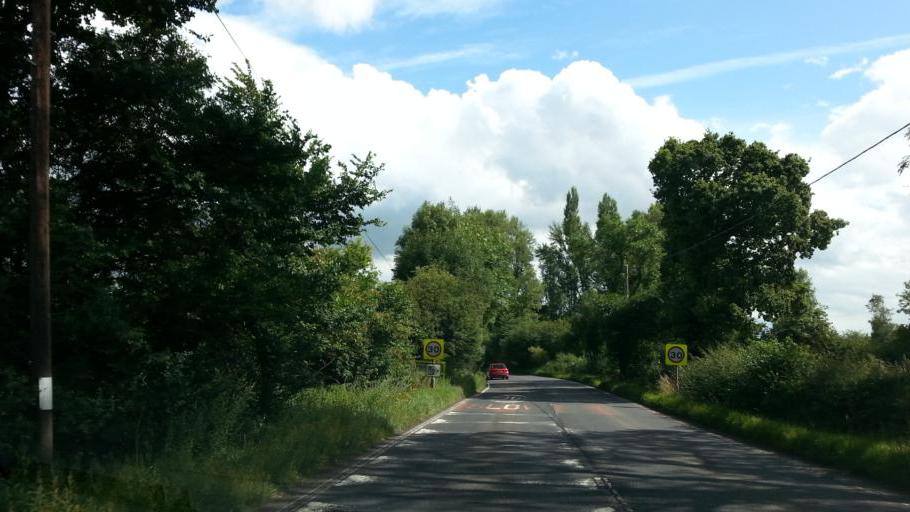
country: GB
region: England
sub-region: Nottinghamshire
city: Farnsfield
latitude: 53.1136
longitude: -0.9911
